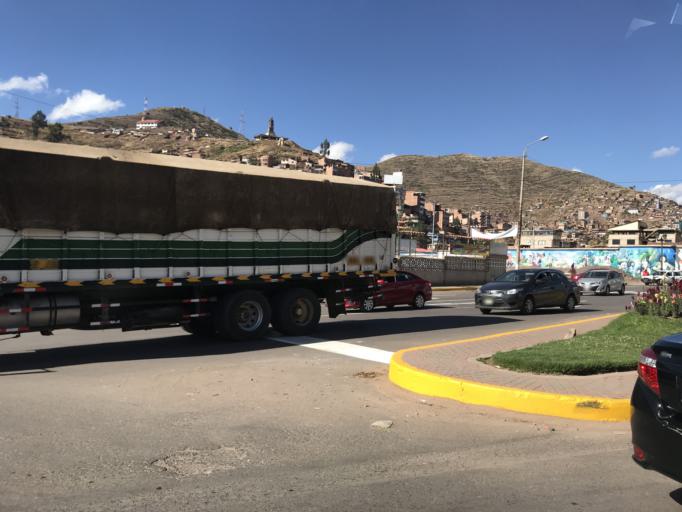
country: PE
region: Cusco
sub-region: Provincia de Cusco
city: Cusco
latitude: -13.5318
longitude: -71.9670
